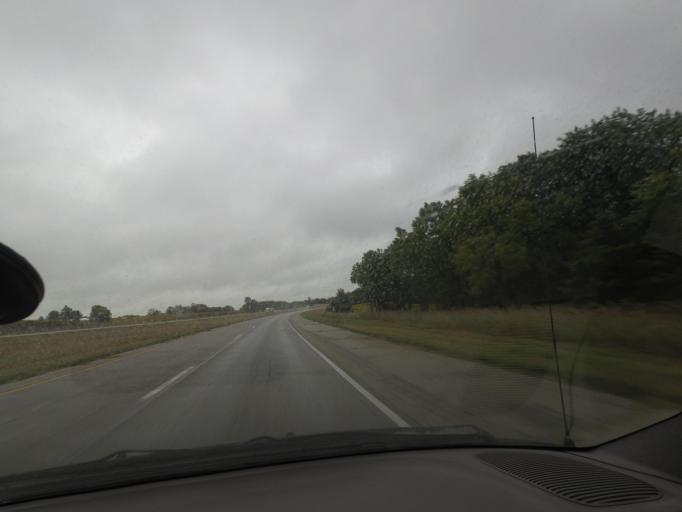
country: US
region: Illinois
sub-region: Pike County
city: Barry
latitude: 39.7390
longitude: -91.1305
